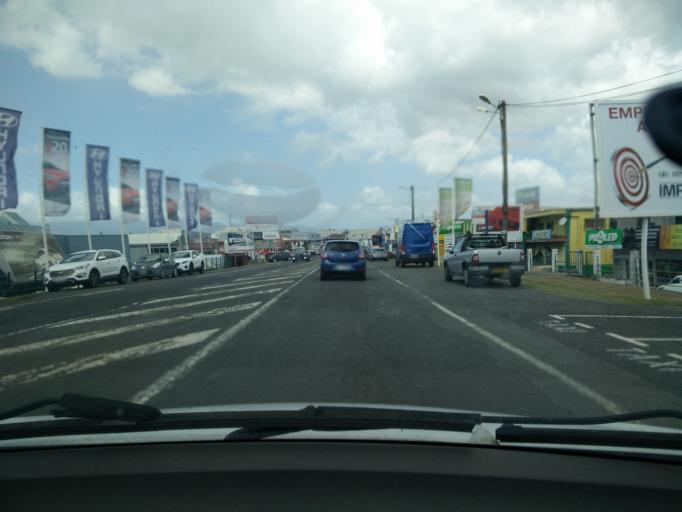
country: GP
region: Guadeloupe
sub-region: Guadeloupe
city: Pointe-a-Pitre
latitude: 16.2418
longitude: -61.5638
